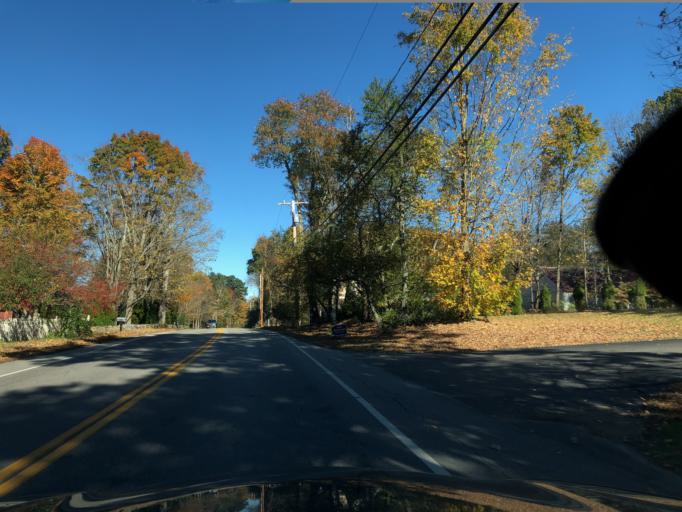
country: US
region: New Hampshire
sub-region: Rockingham County
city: Exeter
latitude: 43.0242
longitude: -70.9435
